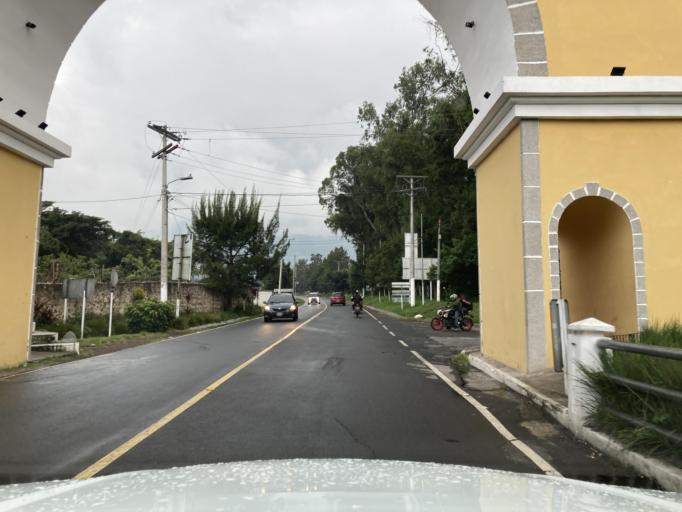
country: GT
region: Sacatepequez
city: San Miguel Duenas
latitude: 14.5222
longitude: -90.7923
